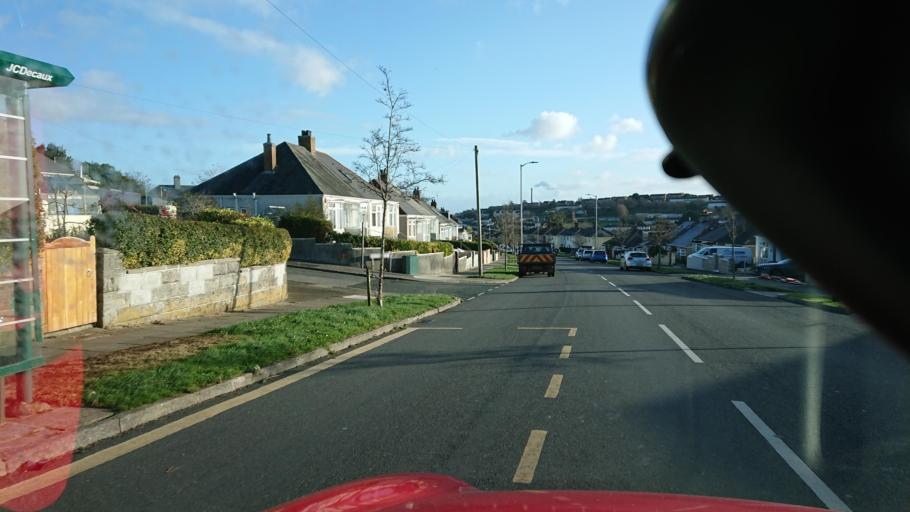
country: GB
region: England
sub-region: Cornwall
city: Saltash
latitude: 50.4057
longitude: -4.1962
